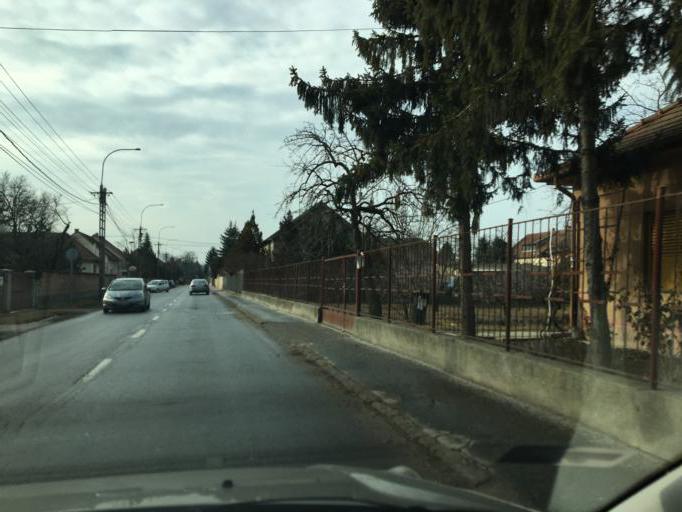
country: HU
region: Pest
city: Szigetszentmiklos
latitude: 47.3447
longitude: 19.0469
